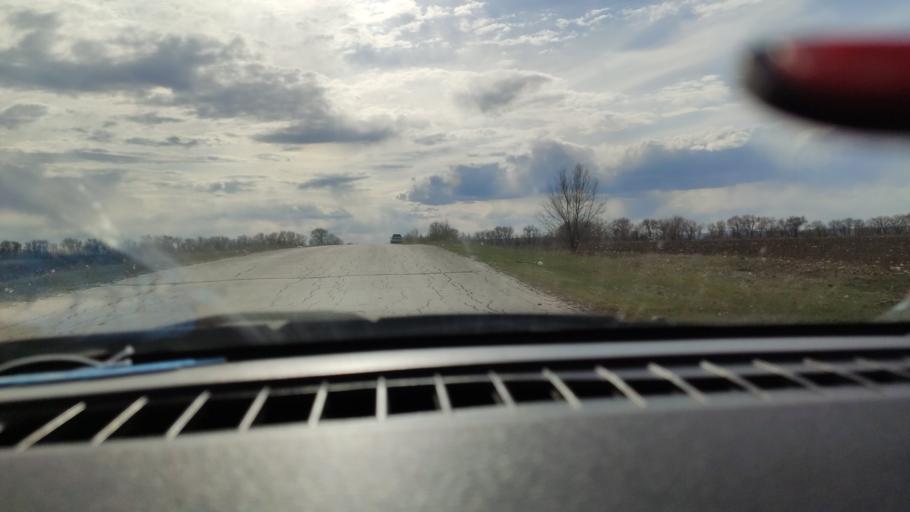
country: RU
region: Saratov
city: Rovnoye
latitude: 50.9392
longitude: 46.1175
